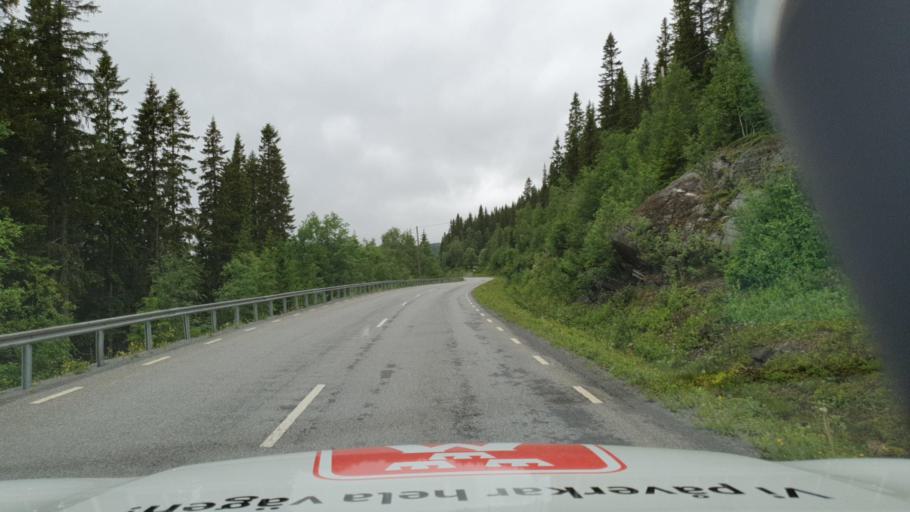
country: SE
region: Jaemtland
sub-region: Are Kommun
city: Are
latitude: 63.5192
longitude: 13.1222
